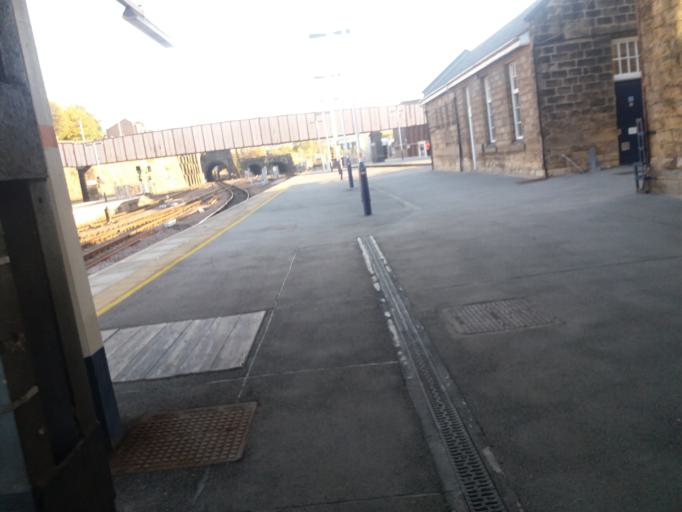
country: GB
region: England
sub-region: Sheffield
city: Sheffield
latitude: 53.3773
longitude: -1.4620
